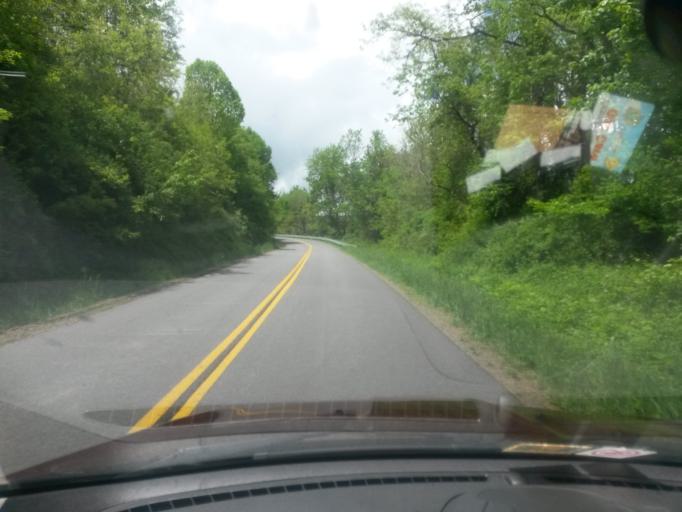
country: US
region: Virginia
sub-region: Floyd County
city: Floyd
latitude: 36.7852
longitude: -80.3854
